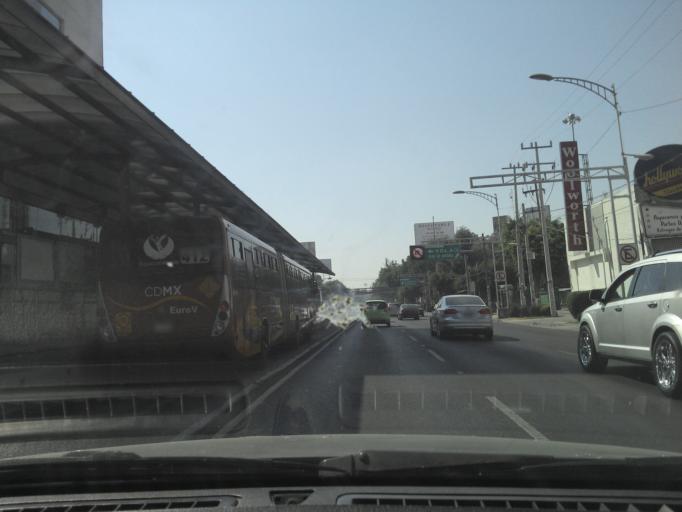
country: MX
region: Mexico City
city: Benito Juarez
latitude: 19.3969
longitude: -99.1560
